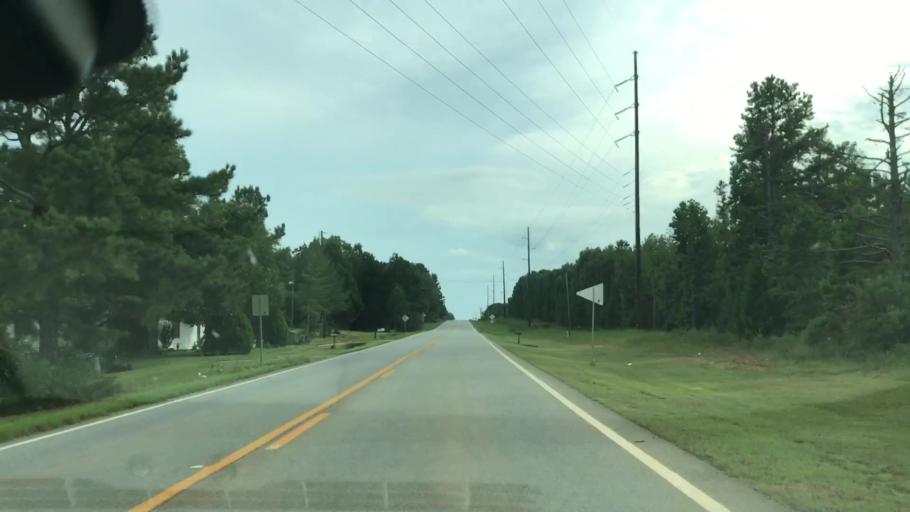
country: US
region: Georgia
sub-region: Quitman County
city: Georgetown
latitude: 31.8451
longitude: -85.0758
